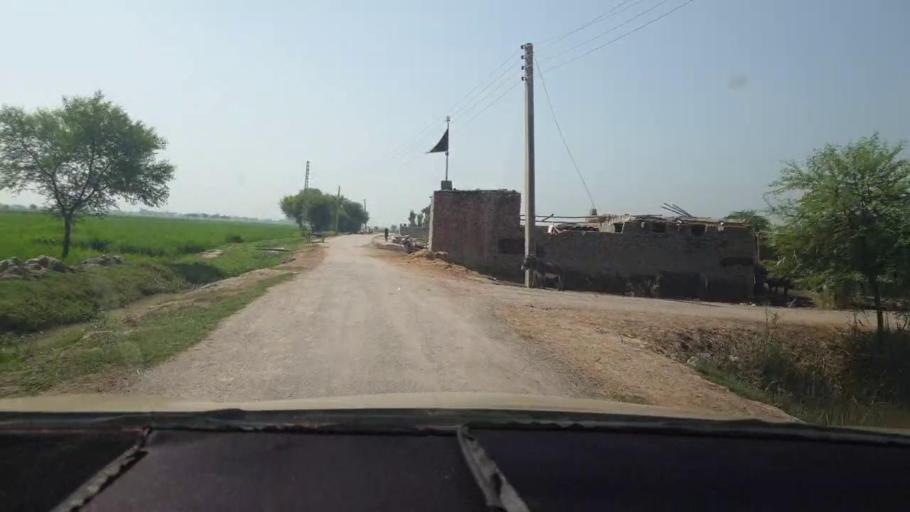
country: PK
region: Sindh
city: Kambar
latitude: 27.5700
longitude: 68.0440
